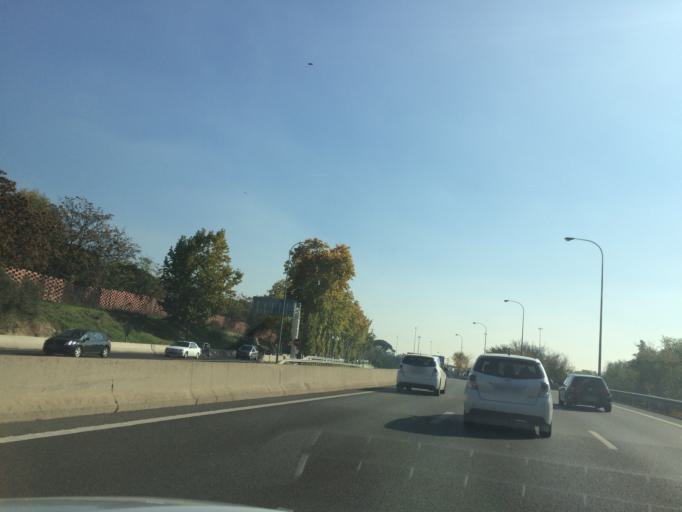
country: ES
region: Madrid
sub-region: Provincia de Madrid
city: Moncloa-Aravaca
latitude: 40.4587
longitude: -3.7452
